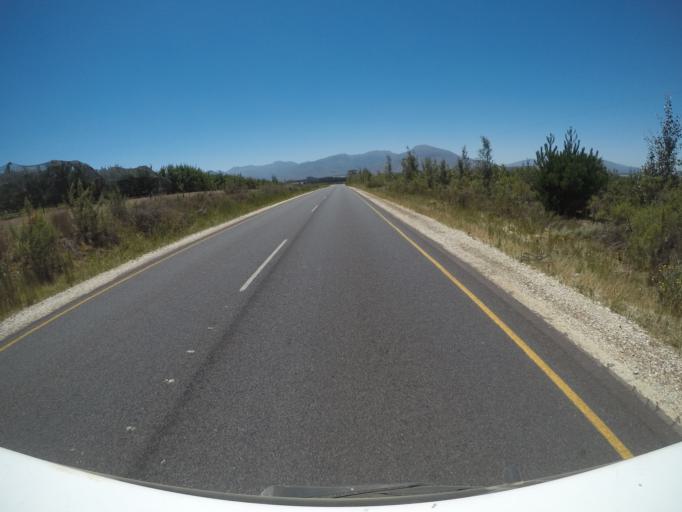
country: ZA
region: Western Cape
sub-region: Overberg District Municipality
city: Grabouw
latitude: -34.0636
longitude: 19.1343
